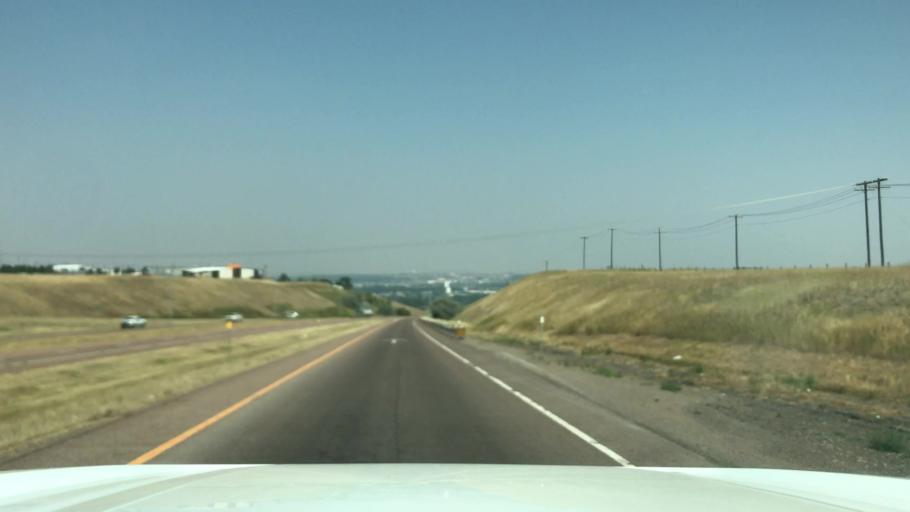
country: US
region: Montana
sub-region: Cascade County
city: Great Falls
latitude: 47.4727
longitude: -111.3595
